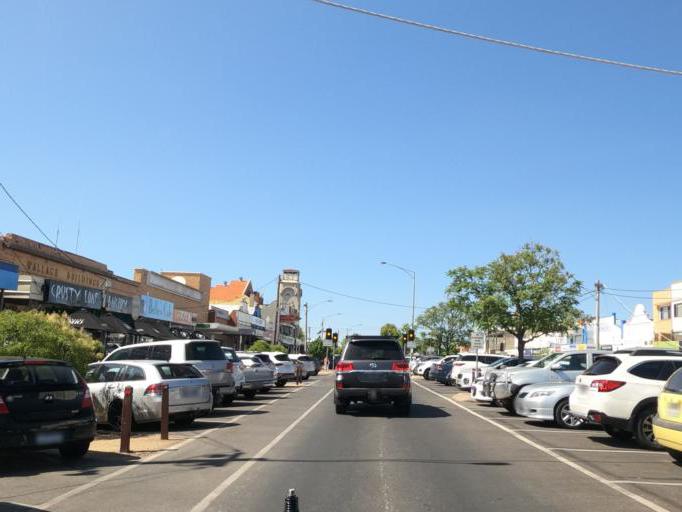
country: AU
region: Victoria
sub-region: Moira
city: Yarrawonga
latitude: -36.0115
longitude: 146.0045
